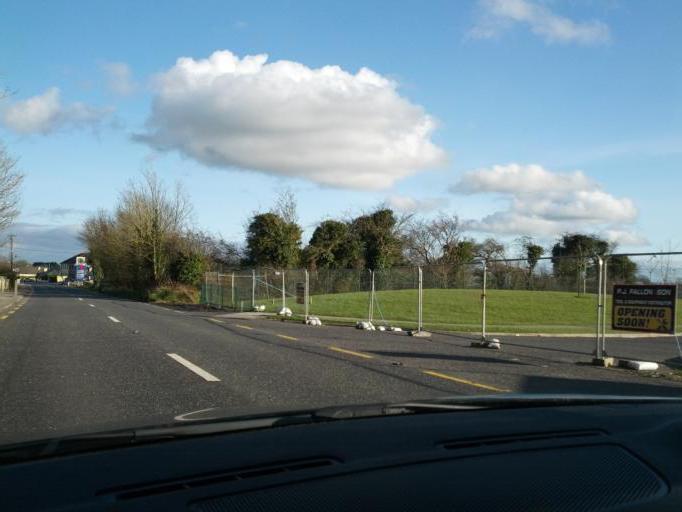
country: IE
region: Connaught
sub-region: Roscommon
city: Roscommon
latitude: 53.6429
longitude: -8.2136
